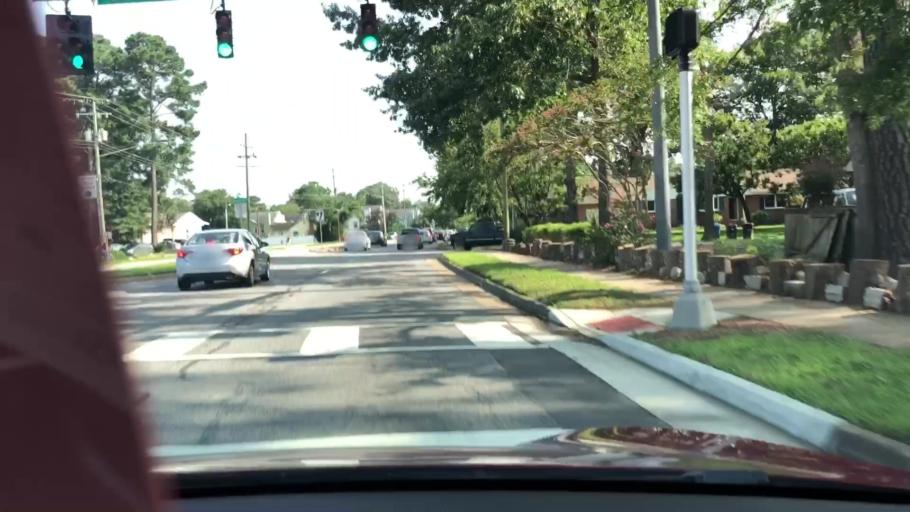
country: US
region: Virginia
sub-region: City of Virginia Beach
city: Virginia Beach
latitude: 36.8524
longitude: -75.9947
